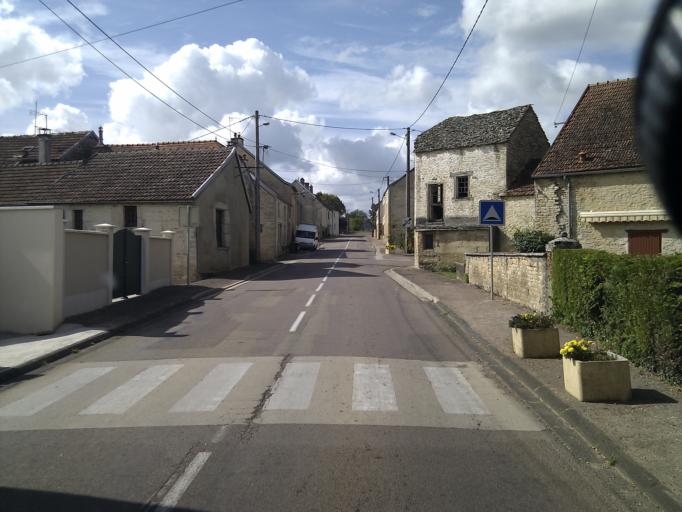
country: FR
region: Bourgogne
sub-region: Departement de la Cote-d'Or
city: Chatillon-sur-Seine
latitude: 47.9159
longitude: 4.6616
